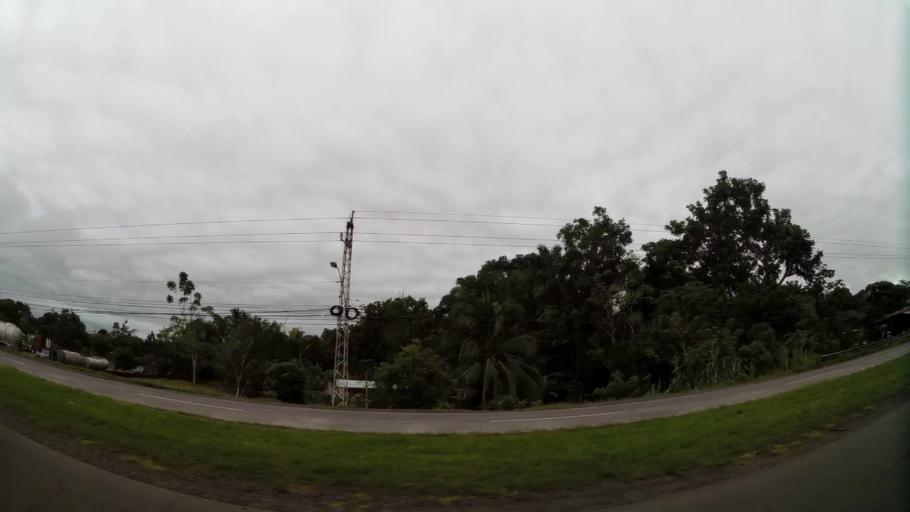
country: PA
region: Chiriqui
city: Boqueron
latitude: 8.4887
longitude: -82.5733
